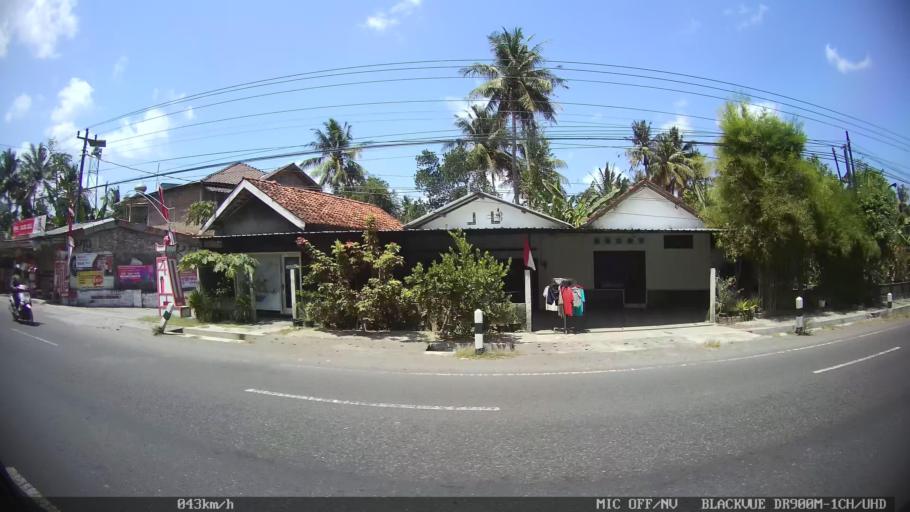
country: ID
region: Daerah Istimewa Yogyakarta
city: Pandak
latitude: -7.9114
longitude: 110.2918
